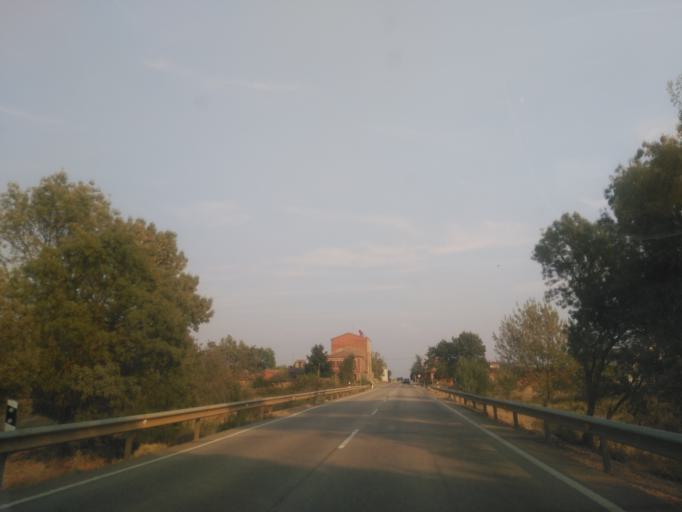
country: ES
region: Castille and Leon
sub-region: Provincia de Zamora
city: Tabara
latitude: 41.8226
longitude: -5.9526
